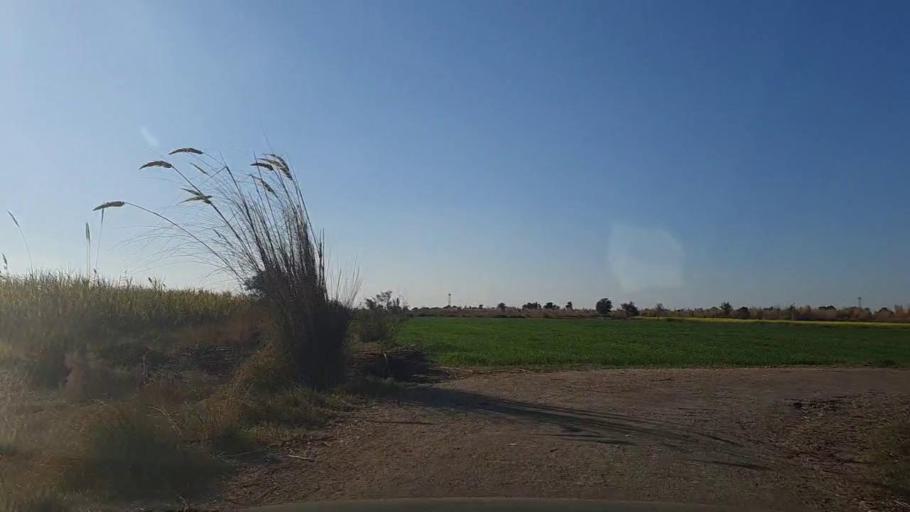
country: PK
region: Sindh
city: Khadro
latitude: 26.2413
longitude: 68.8644
